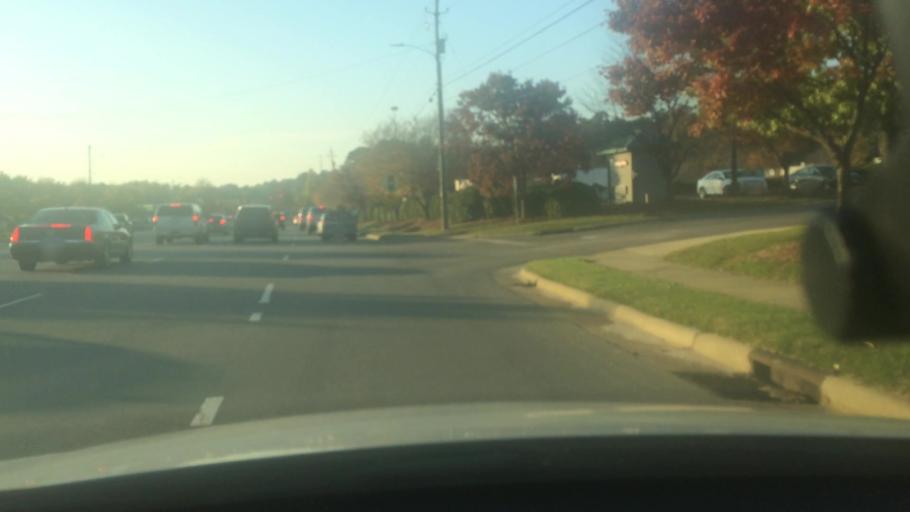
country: US
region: North Carolina
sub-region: Wake County
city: Raleigh
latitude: 35.8191
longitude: -78.6218
